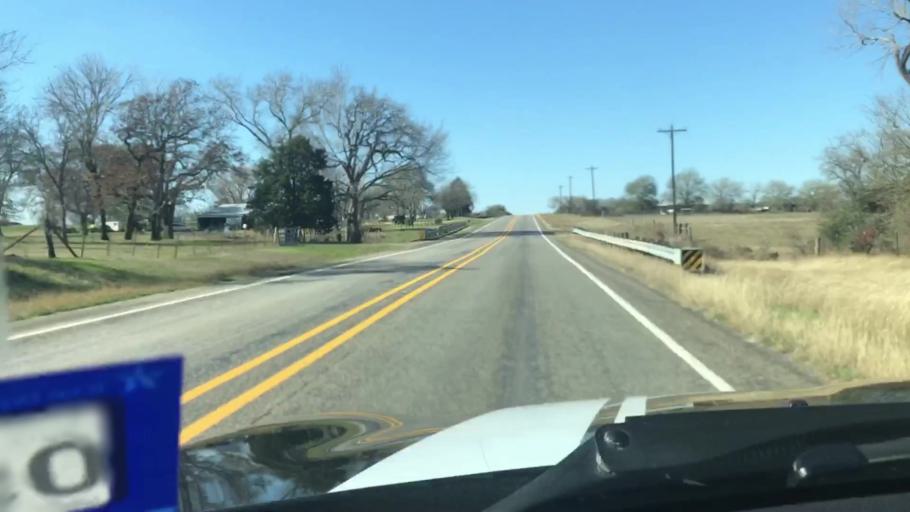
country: US
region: Texas
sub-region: Robertson County
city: Calvert
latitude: 30.8847
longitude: -96.7673
